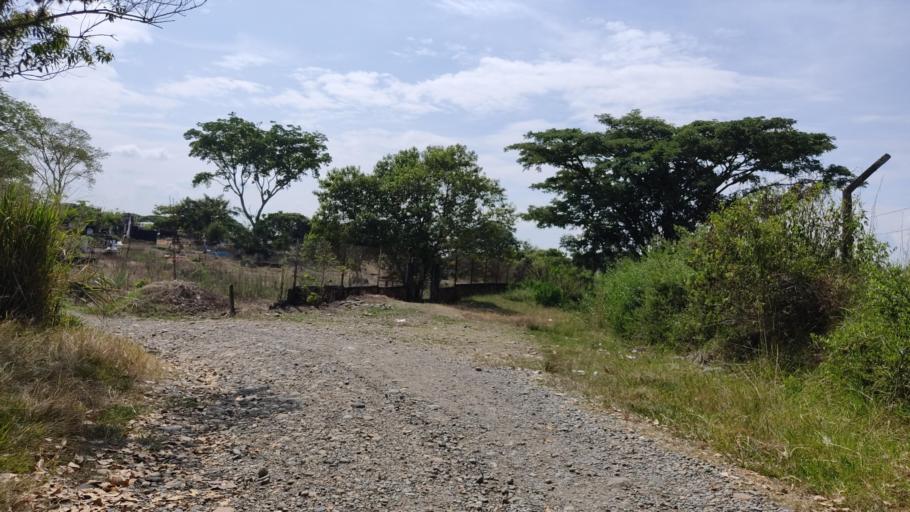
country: CO
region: Cauca
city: Buenos Aires
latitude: 3.1356
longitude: -76.5900
